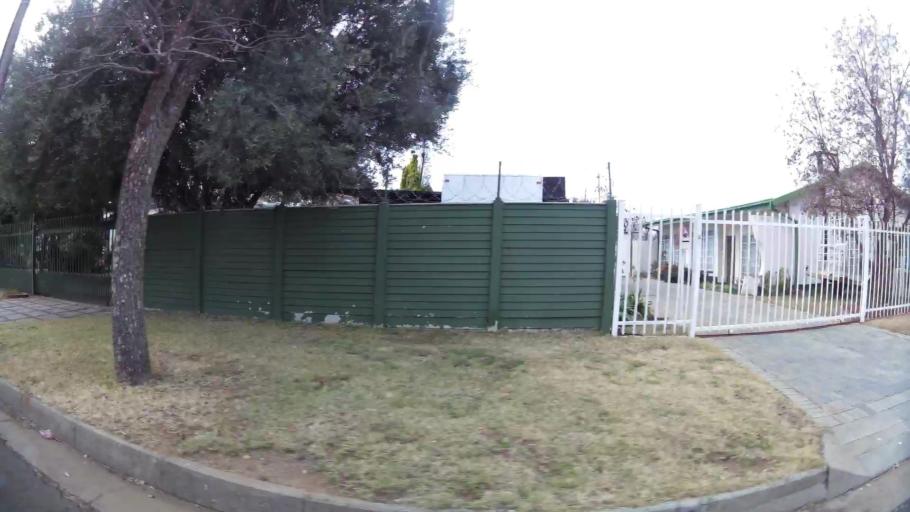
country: ZA
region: Orange Free State
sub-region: Fezile Dabi District Municipality
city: Kroonstad
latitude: -27.6327
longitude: 27.2321
